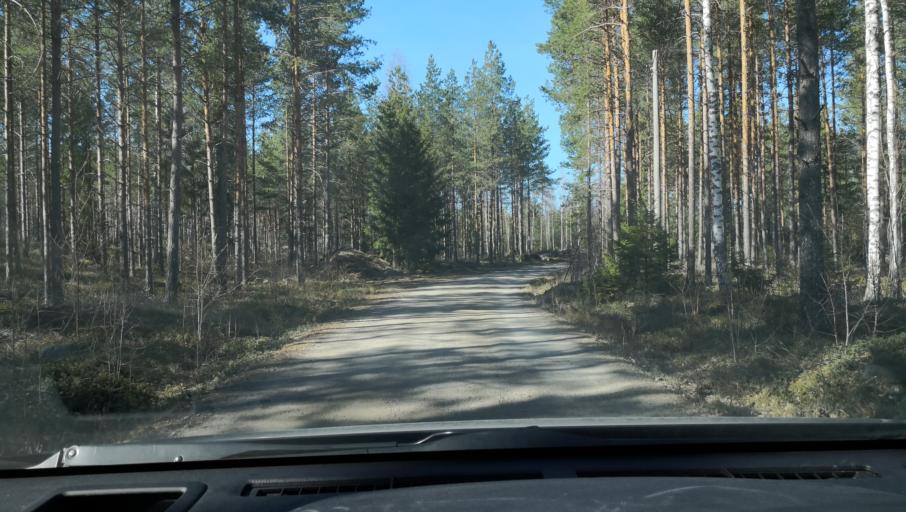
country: SE
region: Vaestmanland
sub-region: Sala Kommun
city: Sala
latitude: 59.9333
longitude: 16.4502
